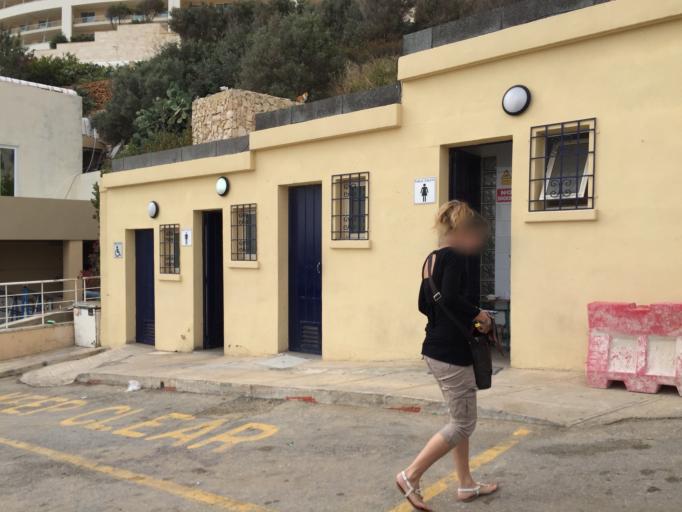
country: MT
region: L-Imgarr
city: Imgarr
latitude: 35.9346
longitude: 14.3447
